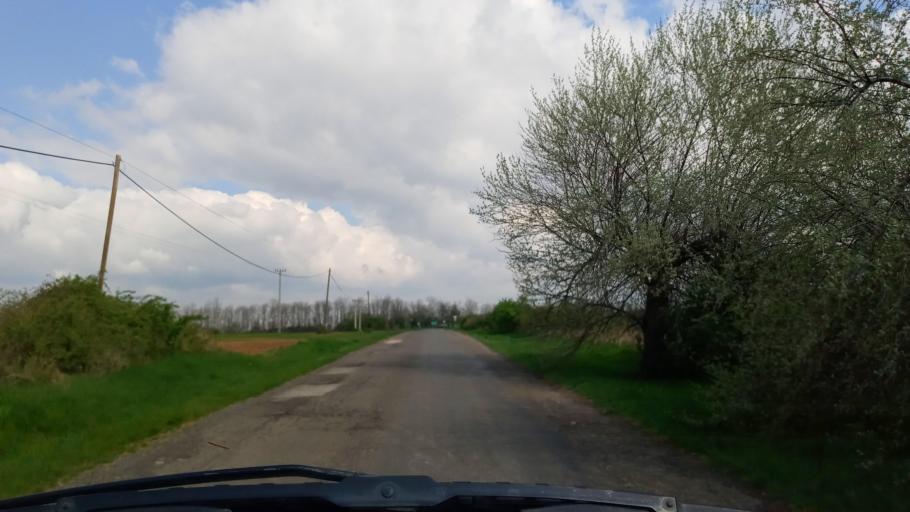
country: HU
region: Baranya
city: Pecsvarad
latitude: 46.1052
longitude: 18.4962
